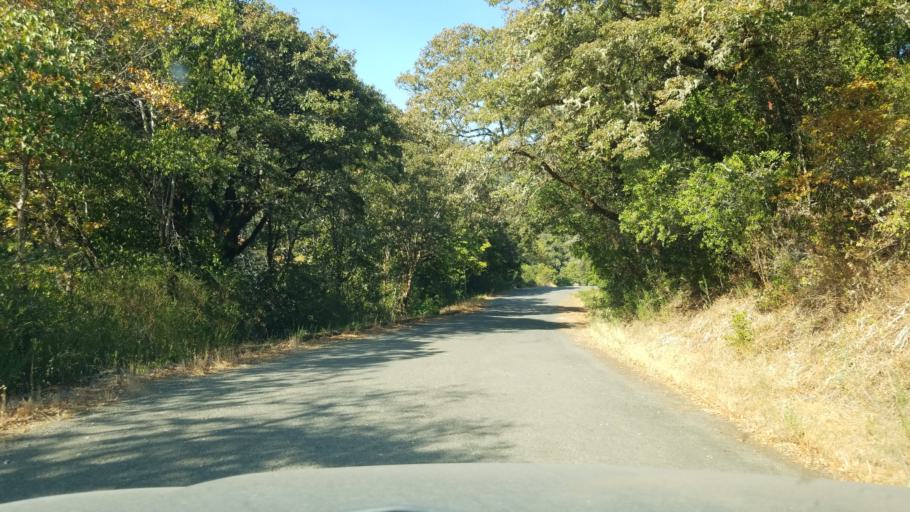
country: US
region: California
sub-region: Humboldt County
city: Redway
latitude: 40.1791
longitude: -123.7812
